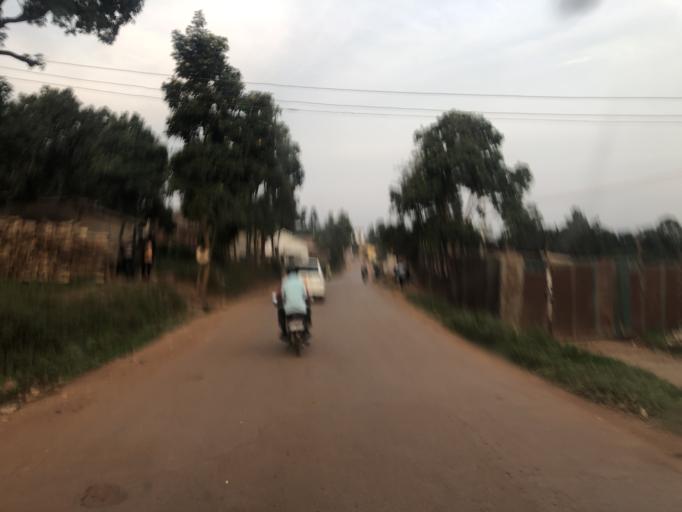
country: UG
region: Central Region
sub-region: Kampala District
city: Kampala
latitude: 0.2731
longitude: 32.5483
